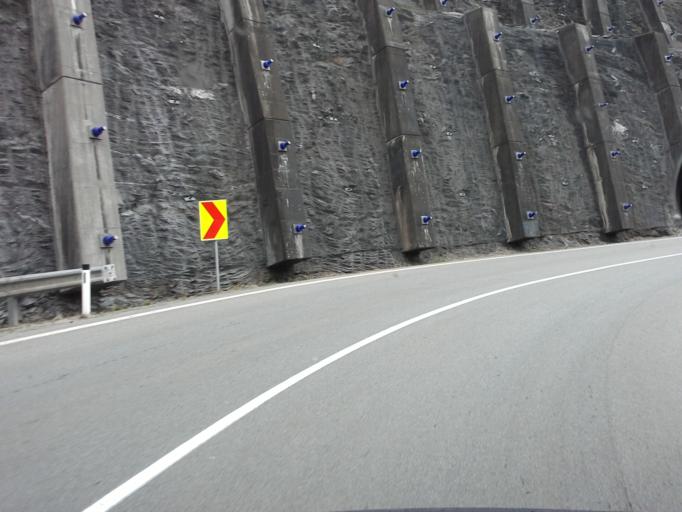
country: AT
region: Tyrol
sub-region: Politischer Bezirk Lienz
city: Matrei in Osttirol
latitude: 47.1198
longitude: 12.4994
